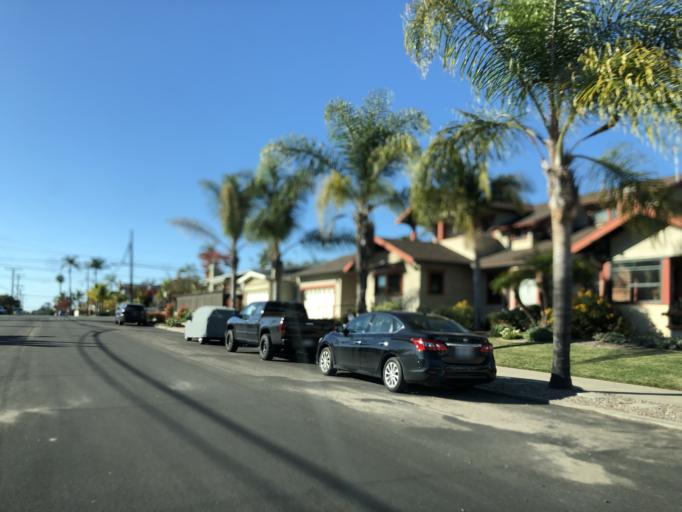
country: US
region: California
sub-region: San Diego County
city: San Diego
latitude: 32.7421
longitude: -117.1319
